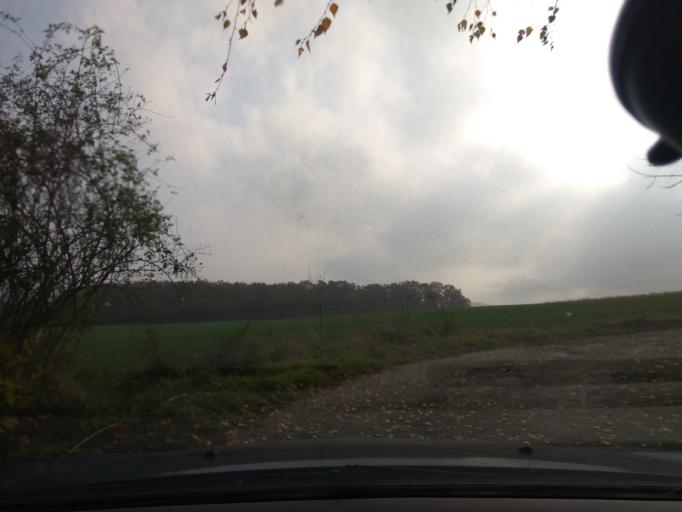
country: SK
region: Trnavsky
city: Vrbove
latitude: 48.6679
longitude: 17.6608
